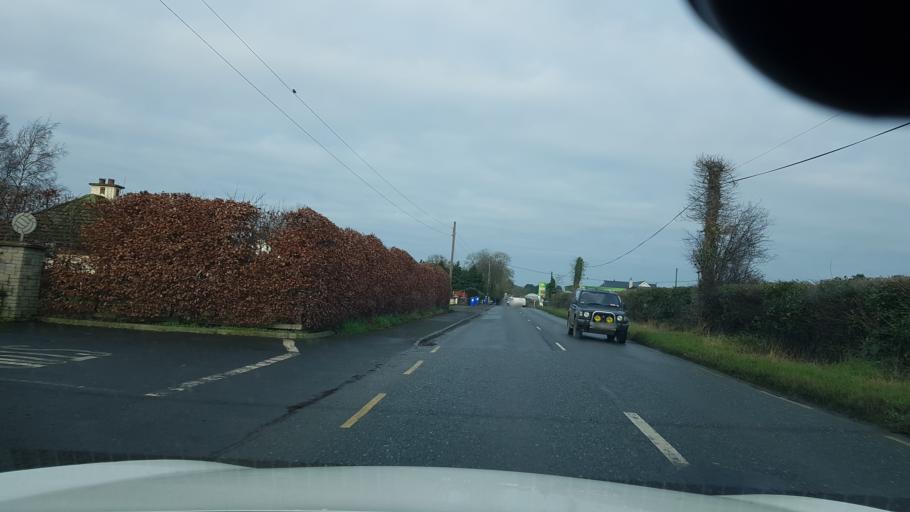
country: IE
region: Leinster
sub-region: An Mhi
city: Navan
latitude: 53.6995
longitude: -6.6797
